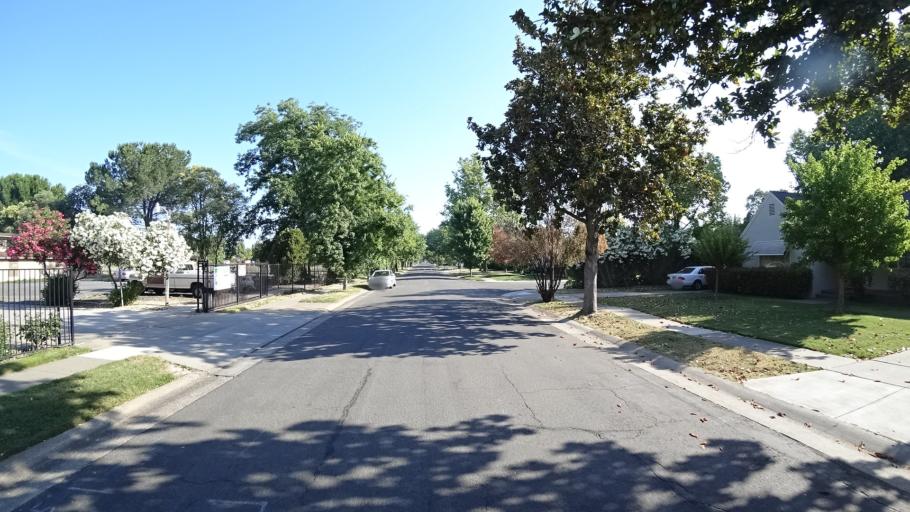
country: US
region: California
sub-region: Sacramento County
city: Florin
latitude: 38.5343
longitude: -121.4311
